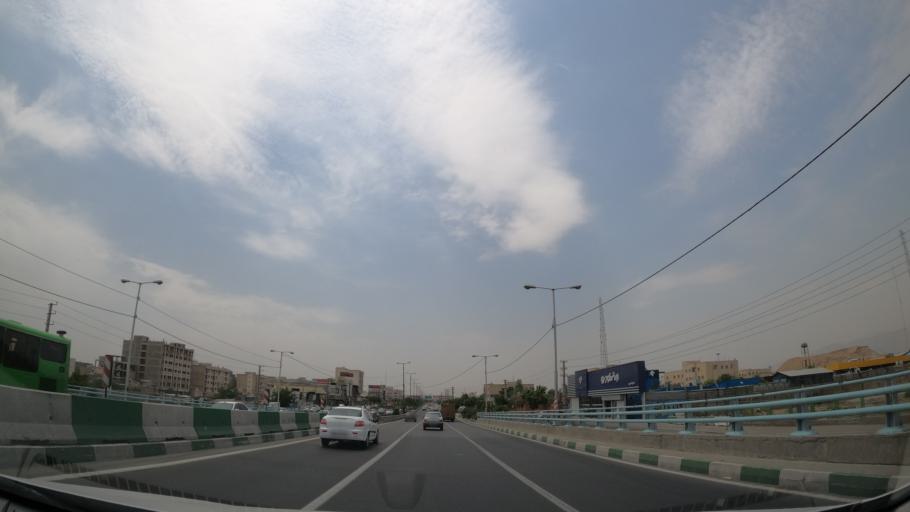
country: IR
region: Tehran
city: Eslamshahr
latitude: 35.6768
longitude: 51.2767
